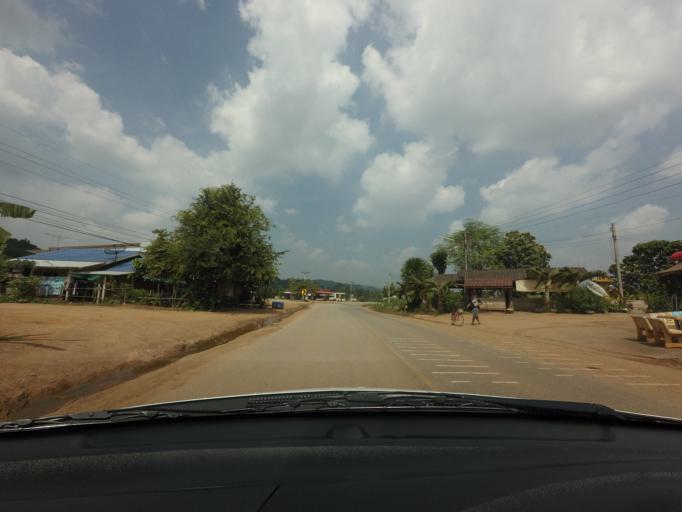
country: TH
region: Nakhon Ratchasima
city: Pak Chong
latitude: 14.5549
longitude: 101.5739
